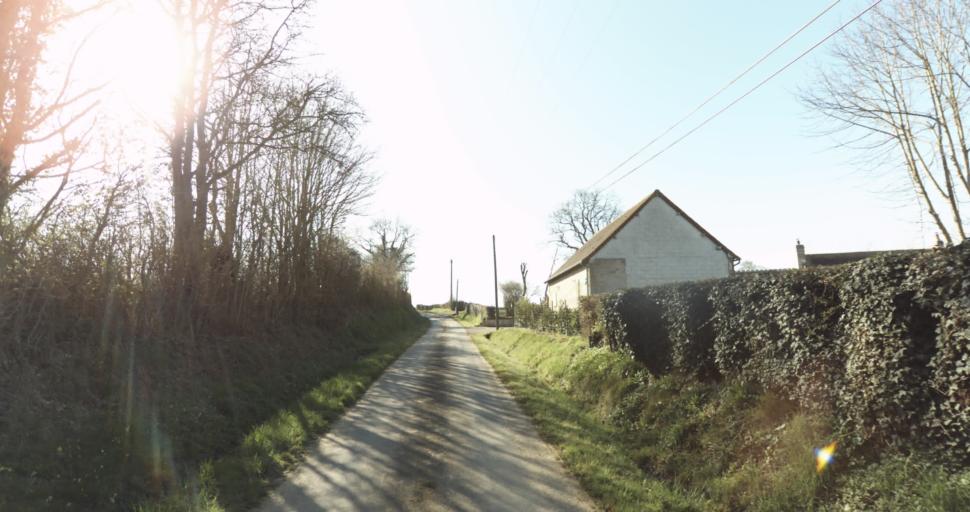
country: FR
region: Lower Normandy
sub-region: Departement du Calvados
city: Saint-Pierre-sur-Dives
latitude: 48.9870
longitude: 0.0134
